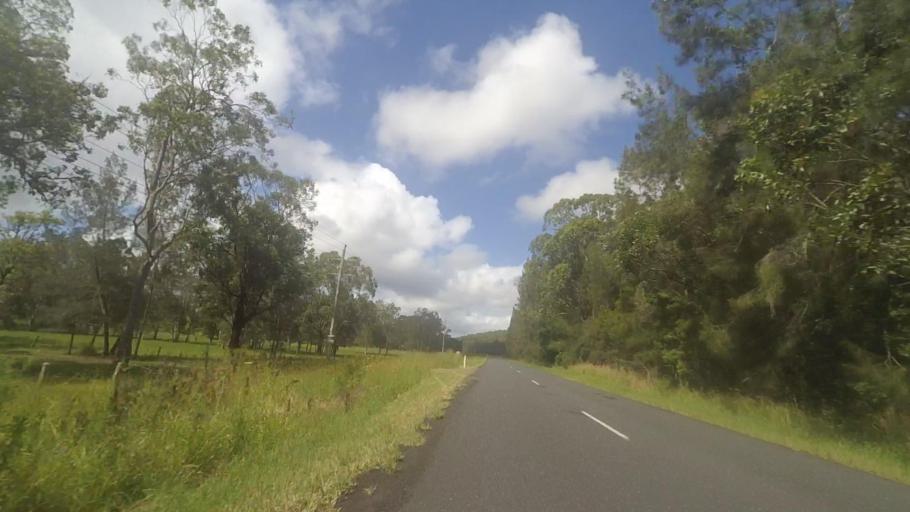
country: AU
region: New South Wales
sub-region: Great Lakes
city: Bulahdelah
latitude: -32.3886
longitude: 152.3334
